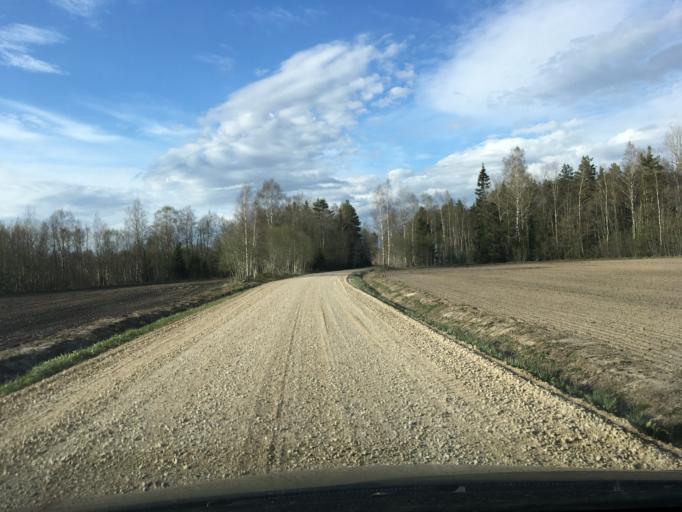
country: EE
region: Raplamaa
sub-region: Maerjamaa vald
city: Marjamaa
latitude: 58.9840
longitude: 24.3628
